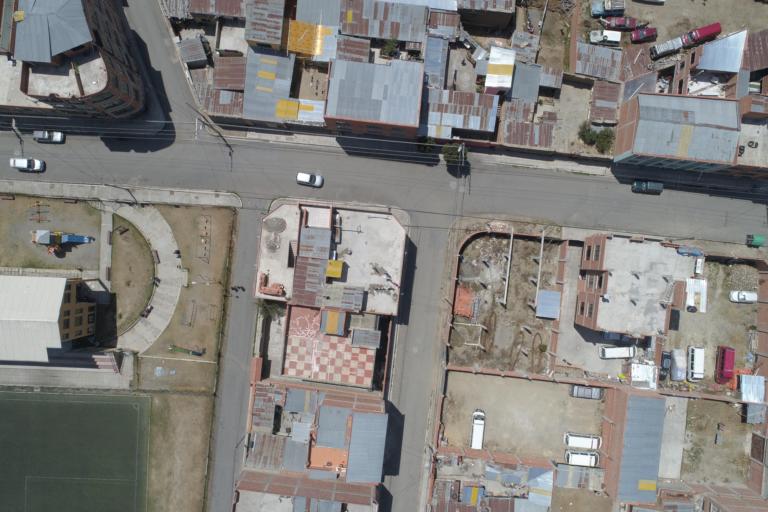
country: BO
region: La Paz
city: La Paz
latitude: -16.5020
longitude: -68.1018
